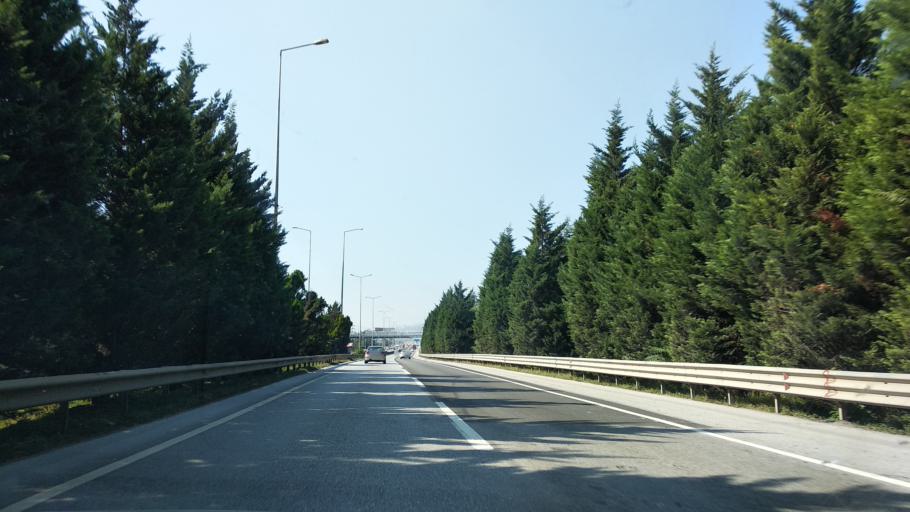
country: TR
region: Kocaeli
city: Kosekoy
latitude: 40.7559
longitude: 30.0064
